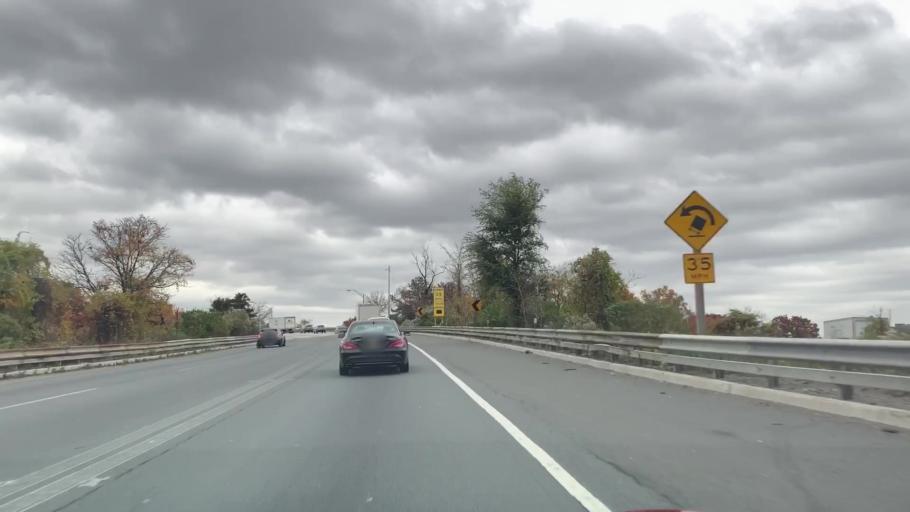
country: US
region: New Jersey
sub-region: Bergen County
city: Ridgefield Park
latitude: 40.8625
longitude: -74.0116
